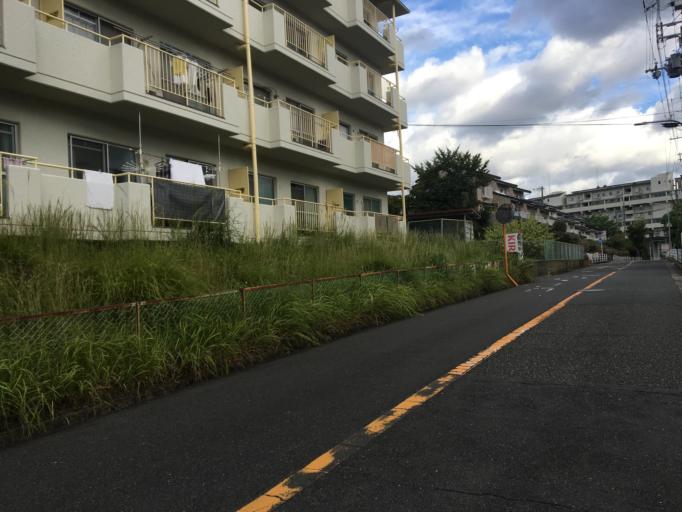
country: JP
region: Osaka
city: Suita
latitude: 34.7984
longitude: 135.5228
